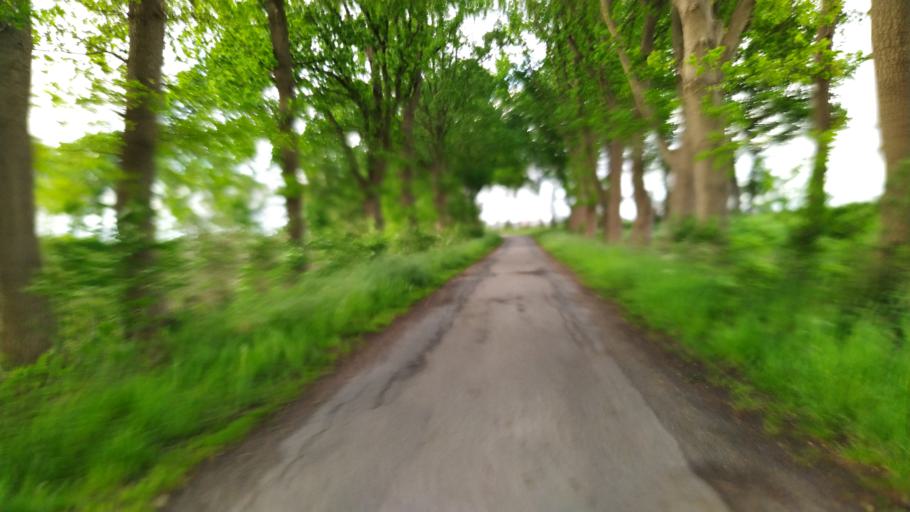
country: DE
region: Lower Saxony
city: Kutenholz
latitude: 53.4713
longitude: 9.3191
